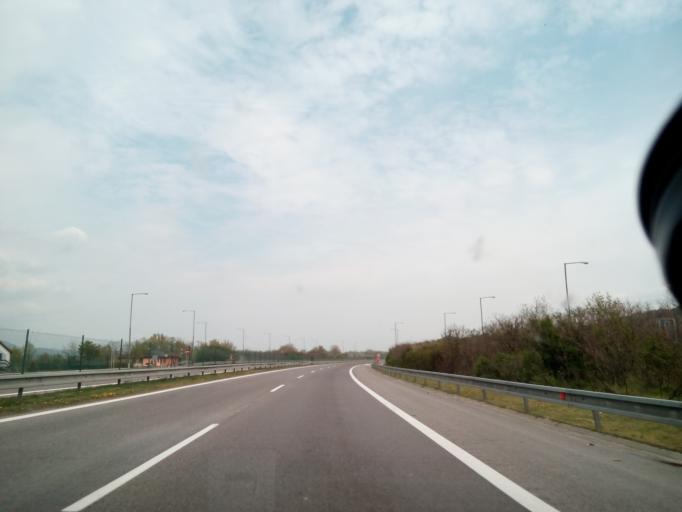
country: SK
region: Trenciansky
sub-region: Okres Nove Mesto nad Vahom
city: Nove Mesto nad Vahom
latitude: 48.7988
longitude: 17.8931
